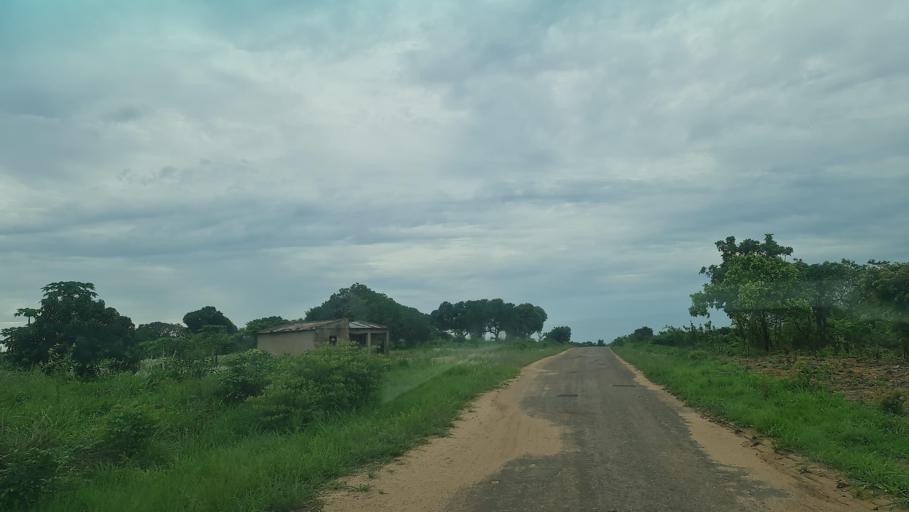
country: MW
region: Southern Region
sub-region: Nsanje District
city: Nsanje
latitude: -17.6943
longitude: 35.7400
